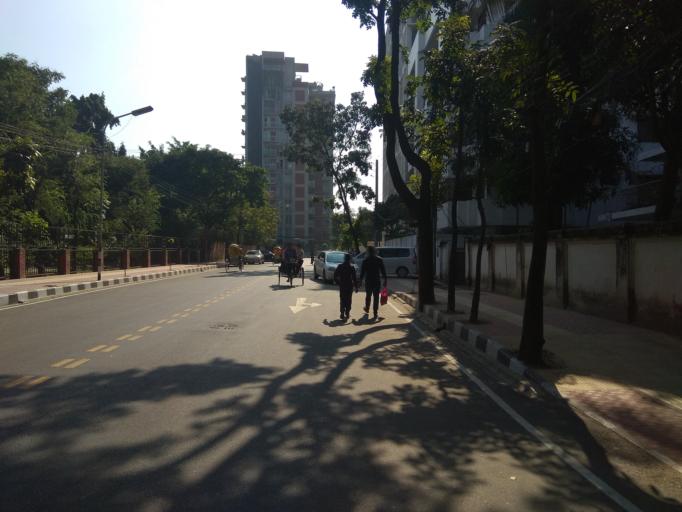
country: BD
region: Dhaka
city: Paltan
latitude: 23.8014
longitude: 90.4080
